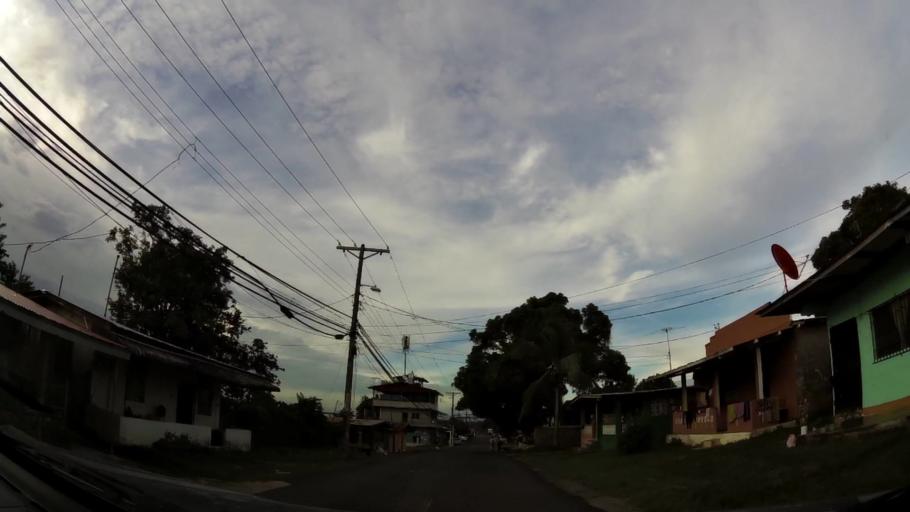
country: PA
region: Panama
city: La Chorrera
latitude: 8.8850
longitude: -79.7817
